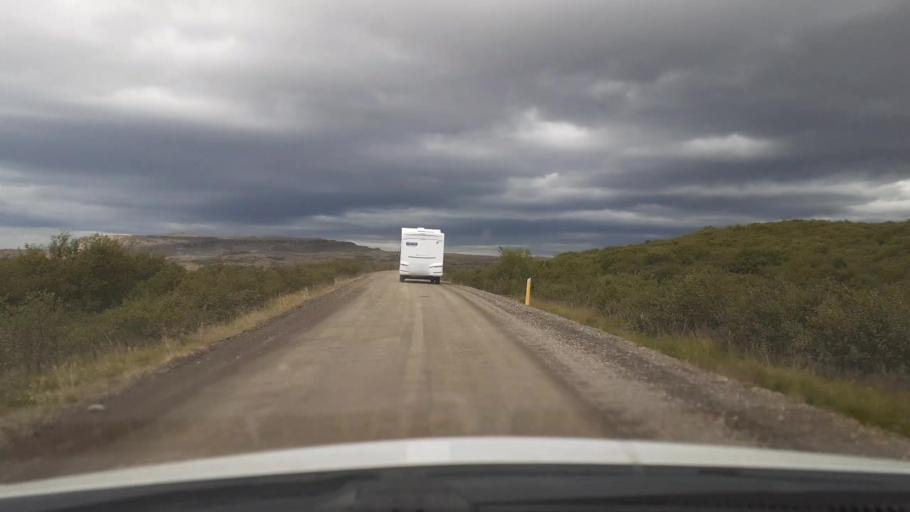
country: IS
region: West
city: Borgarnes
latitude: 64.5517
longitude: -21.6218
